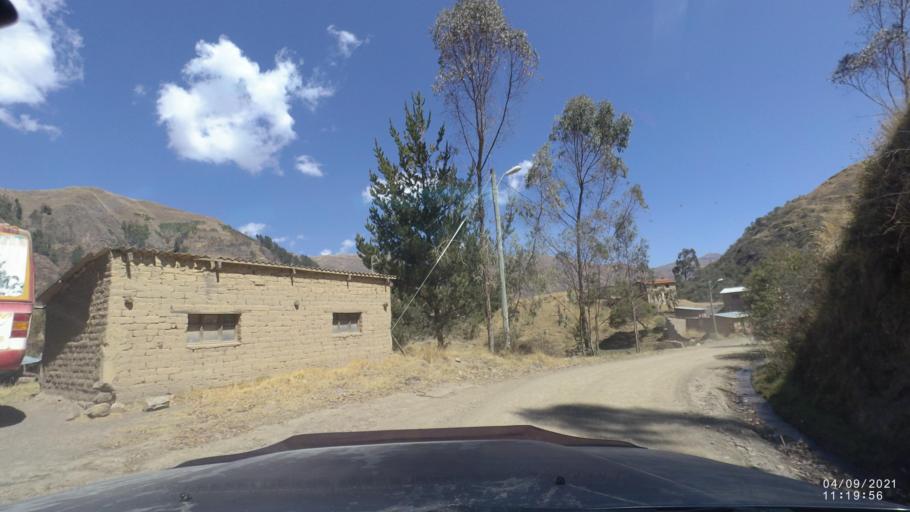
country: BO
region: Cochabamba
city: Sipe Sipe
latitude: -17.2666
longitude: -66.4983
